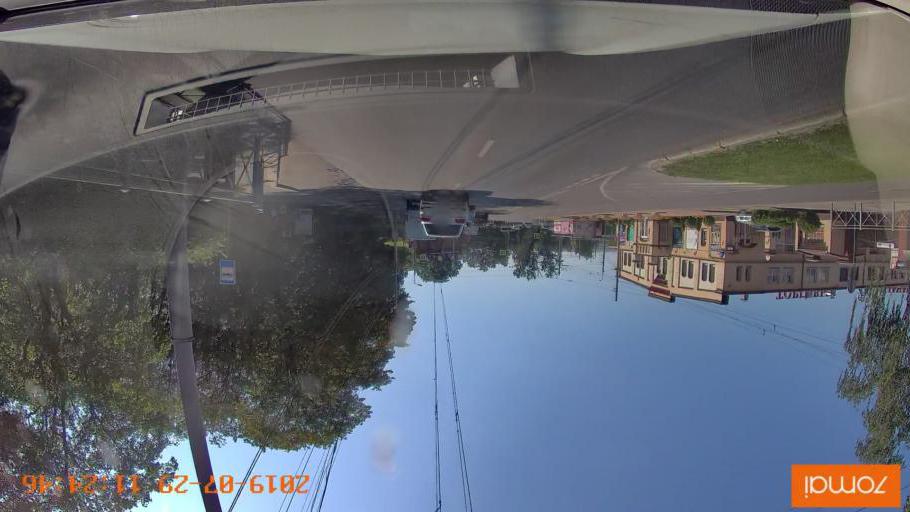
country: RU
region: Kaliningrad
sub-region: Gorod Kaliningrad
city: Kaliningrad
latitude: 54.6956
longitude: 20.5194
